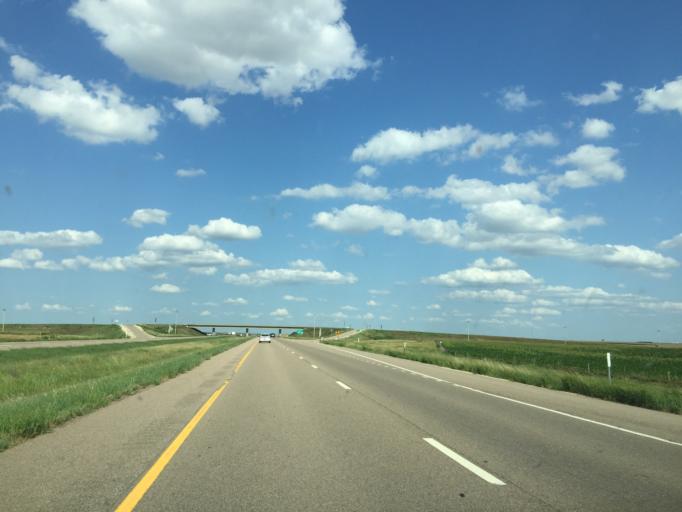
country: US
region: Kansas
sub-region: Gove County
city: Gove
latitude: 39.0971
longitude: -100.3746
